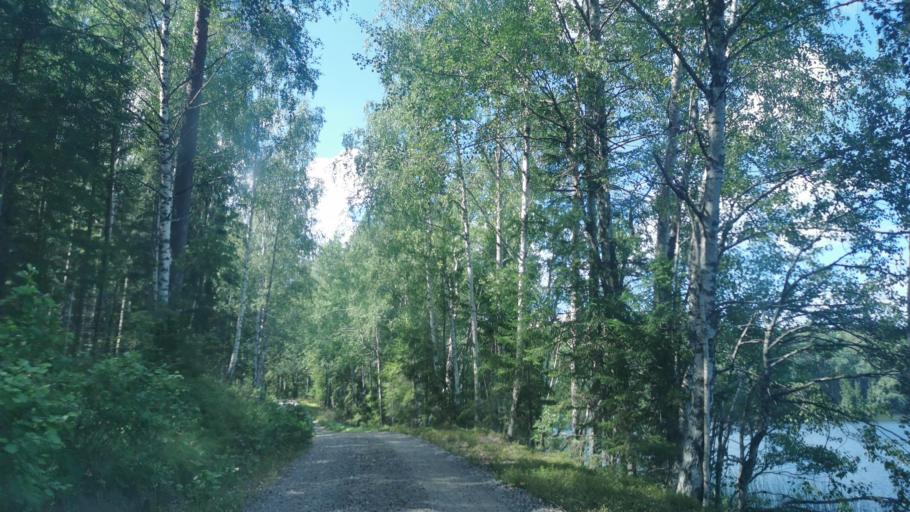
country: SE
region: OEstergoetland
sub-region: Finspangs Kommun
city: Finspang
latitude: 58.7980
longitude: 15.8150
